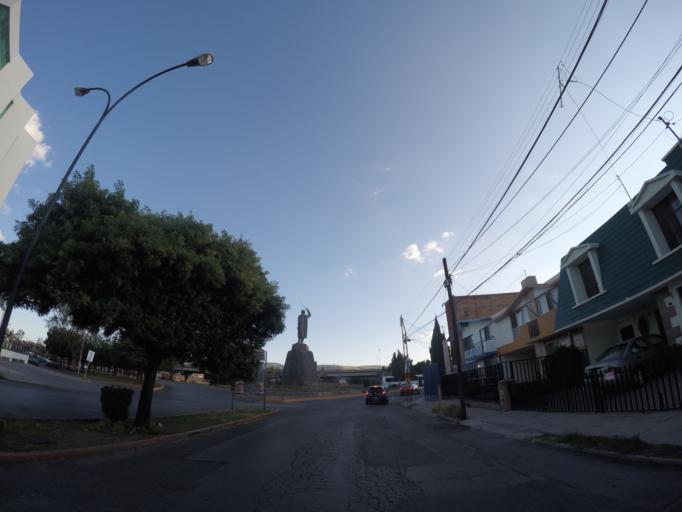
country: MX
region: San Luis Potosi
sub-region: San Luis Potosi
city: San Luis Potosi
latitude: 22.1349
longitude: -100.9893
